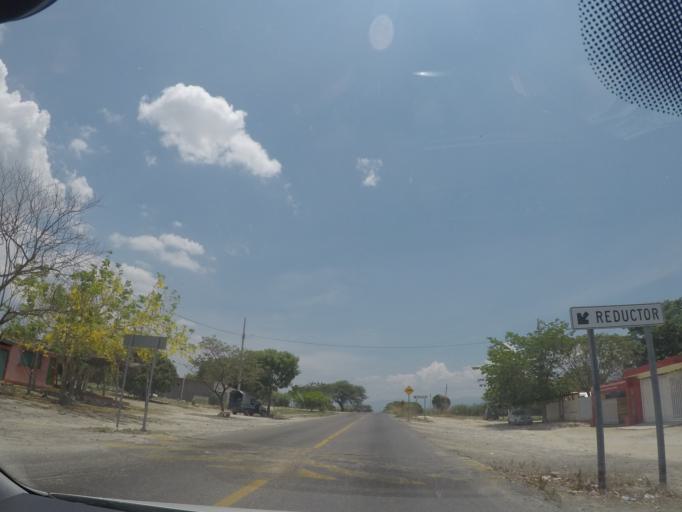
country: MX
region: Oaxaca
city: Santa Maria Jalapa del Marques
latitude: 16.4398
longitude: -95.4657
